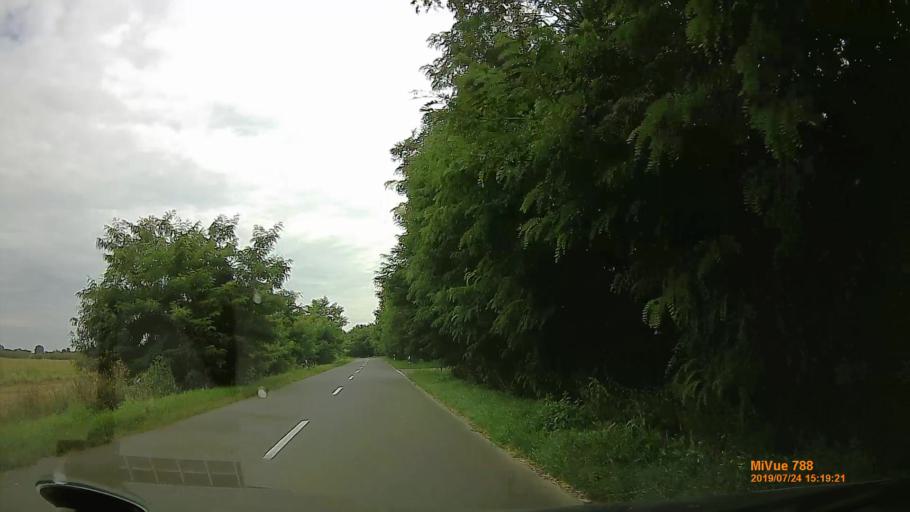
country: HU
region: Szabolcs-Szatmar-Bereg
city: Tarpa
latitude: 48.1708
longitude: 22.5437
